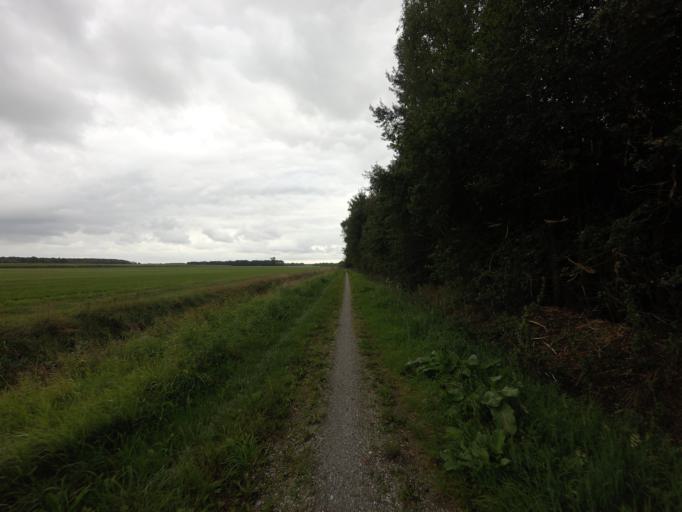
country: NL
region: Friesland
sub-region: Gemeente Weststellingwerf
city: Noordwolde
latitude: 52.9467
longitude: 6.1824
